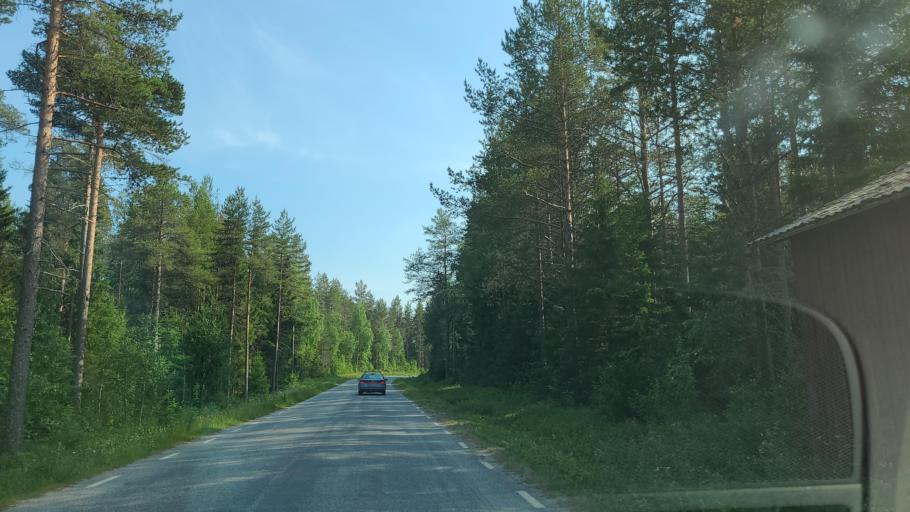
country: SE
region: Vaesterbotten
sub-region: Skelleftea Kommun
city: Burea
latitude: 64.3562
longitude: 21.3379
